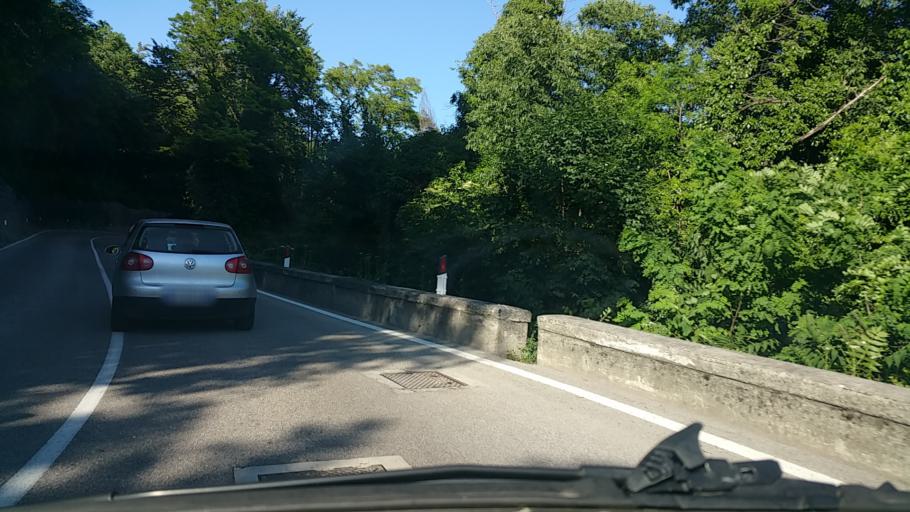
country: IT
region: Trentino-Alto Adige
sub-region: Provincia di Trento
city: Povo
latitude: 46.0707
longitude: 11.1447
